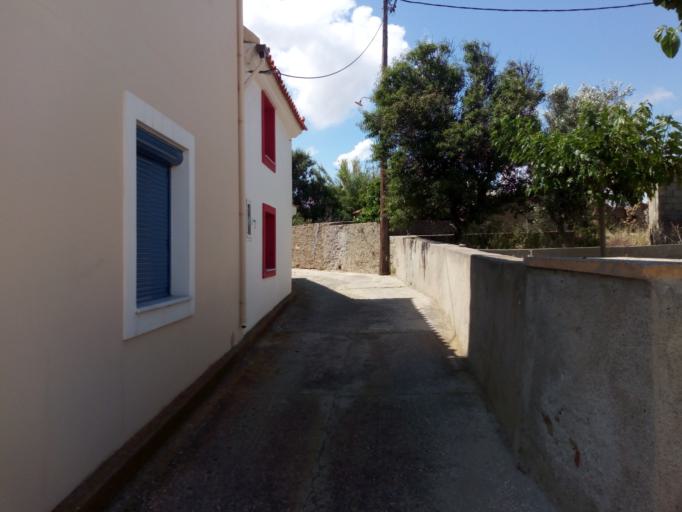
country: GR
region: North Aegean
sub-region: Nomos Lesvou
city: Myrina
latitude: 39.8292
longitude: 25.3281
